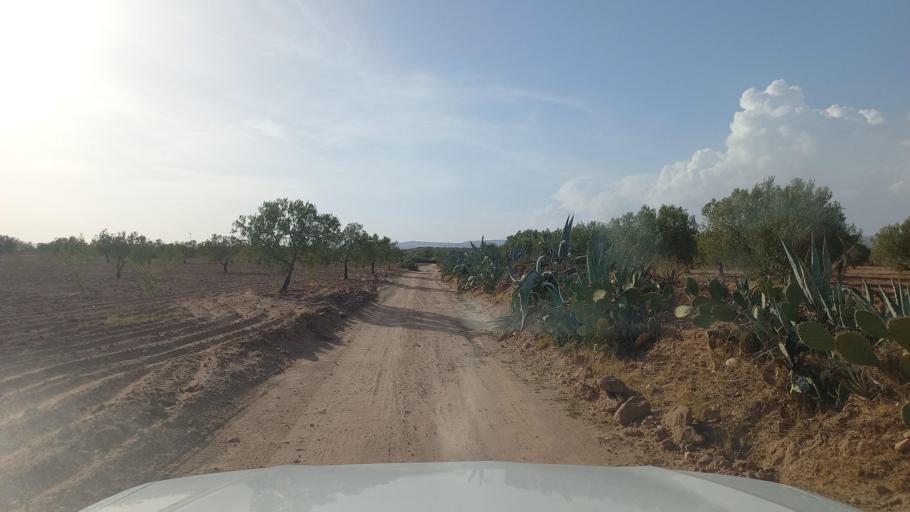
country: TN
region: Al Qasrayn
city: Kasserine
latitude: 35.2307
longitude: 8.9254
